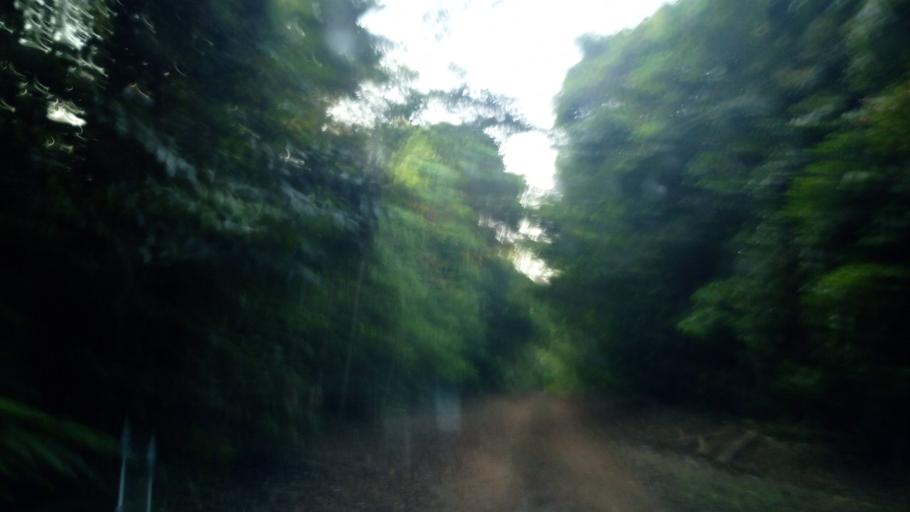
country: AU
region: Queensland
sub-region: Tablelands
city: Atherton
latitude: -17.3782
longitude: 145.7600
